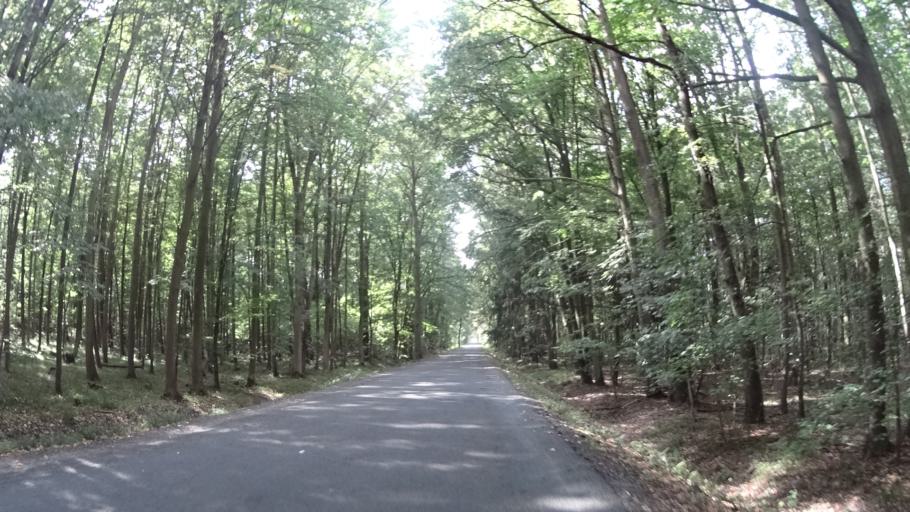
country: CZ
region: Olomoucky
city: Bila Lhota
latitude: 49.7248
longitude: 17.0217
